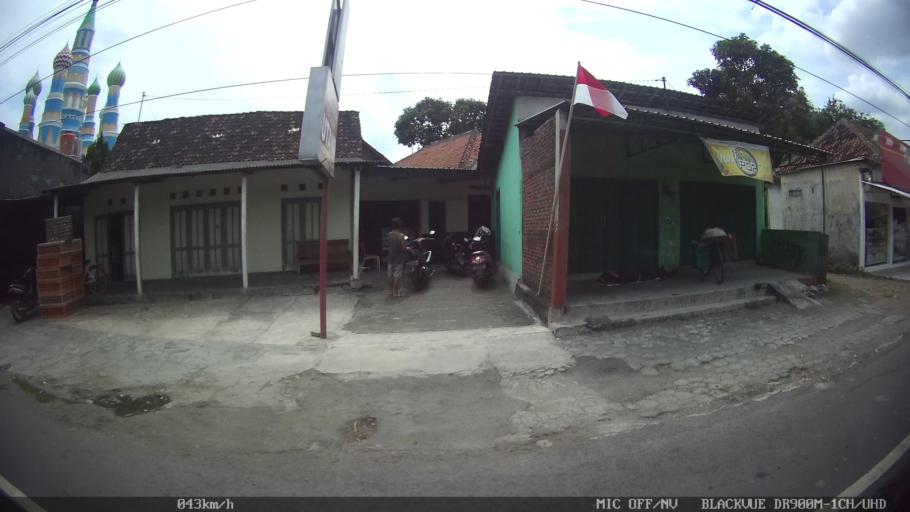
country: ID
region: Central Java
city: Candi Prambanan
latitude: -7.7625
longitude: 110.4754
